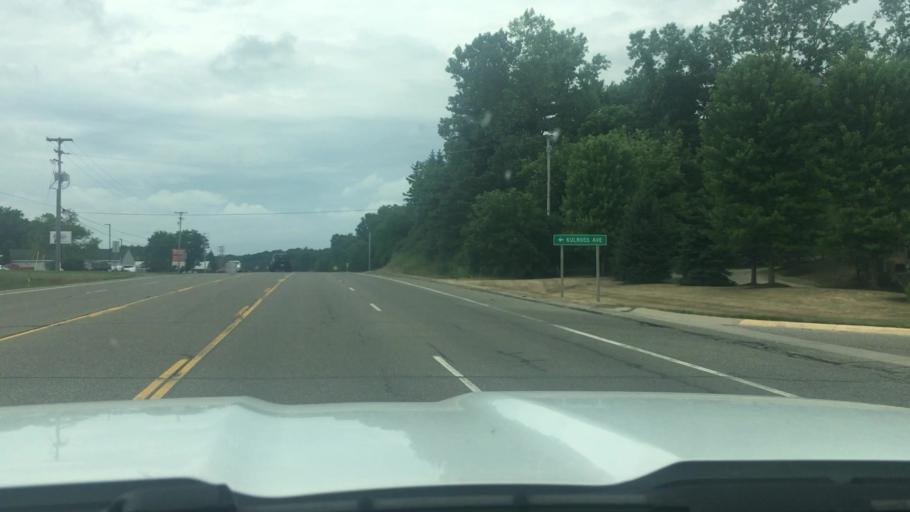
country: US
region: Michigan
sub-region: Kent County
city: Forest Hills
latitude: 42.9612
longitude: -85.5035
